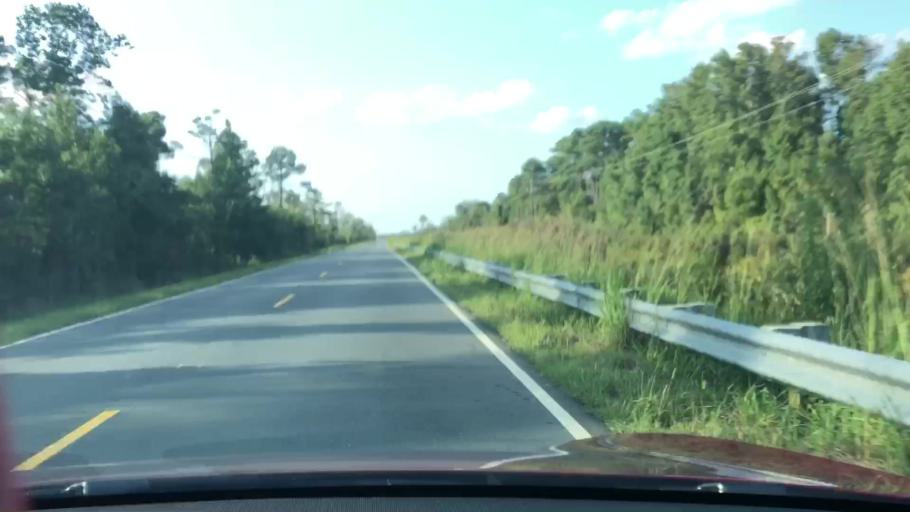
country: US
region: North Carolina
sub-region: Dare County
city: Wanchese
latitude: 35.6721
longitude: -75.7788
